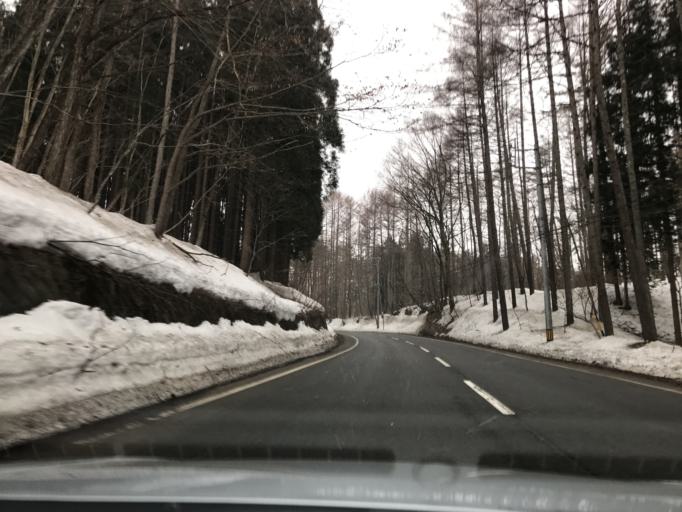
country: JP
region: Nagano
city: Omachi
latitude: 36.5617
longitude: 137.8675
